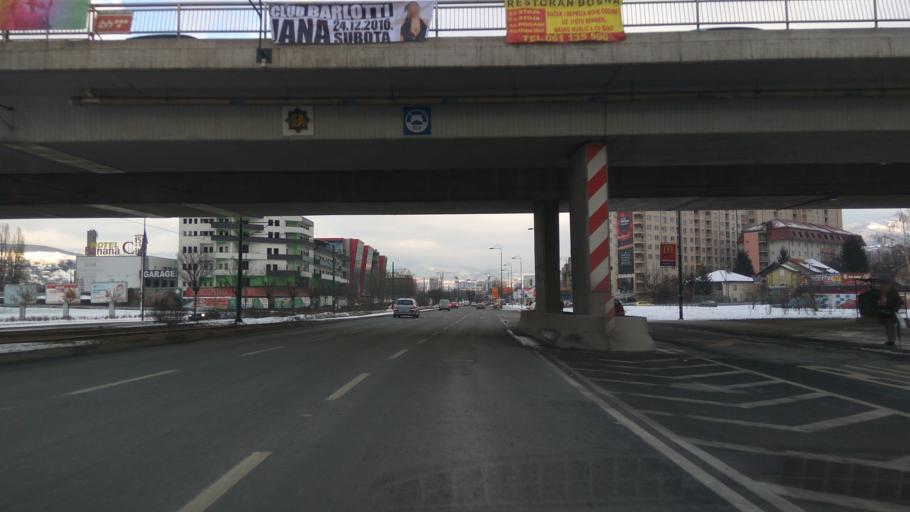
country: BA
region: Federation of Bosnia and Herzegovina
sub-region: Kanton Sarajevo
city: Sarajevo
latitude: 43.8427
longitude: 18.3286
